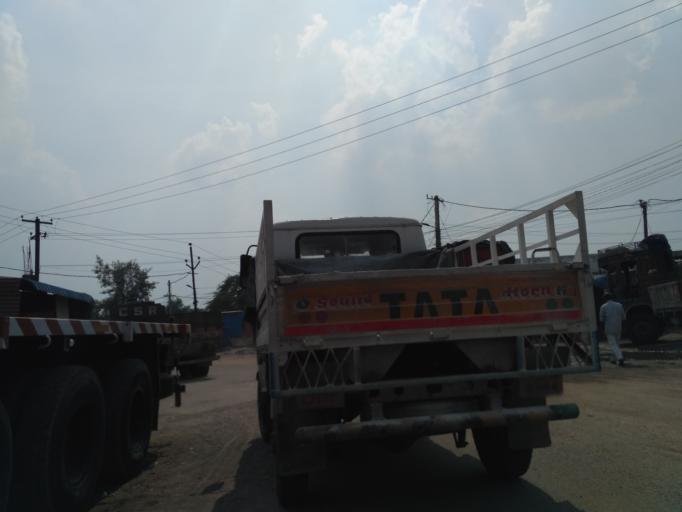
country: IN
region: Telangana
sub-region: Rangareddi
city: Kukatpalli
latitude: 17.4657
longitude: 78.4214
